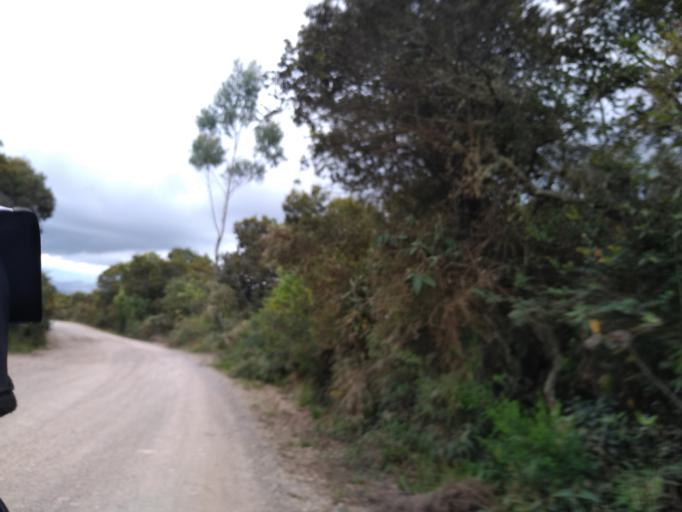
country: CO
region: Boyaca
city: Sotaquira
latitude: 5.7530
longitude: -73.2950
